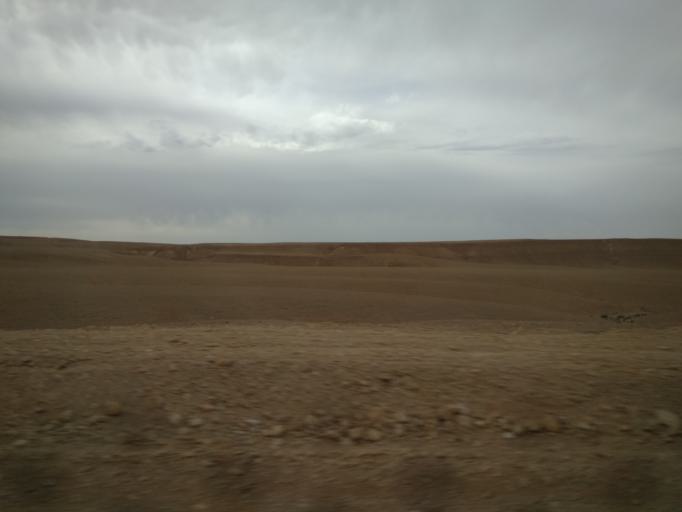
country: IL
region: Southern District
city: Eilat
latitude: 29.8477
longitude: 34.8395
